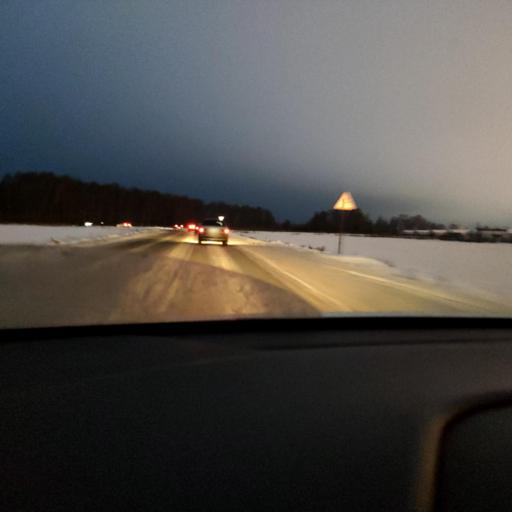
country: RU
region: Tatarstan
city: Osinovo
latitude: 55.8979
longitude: 48.8938
